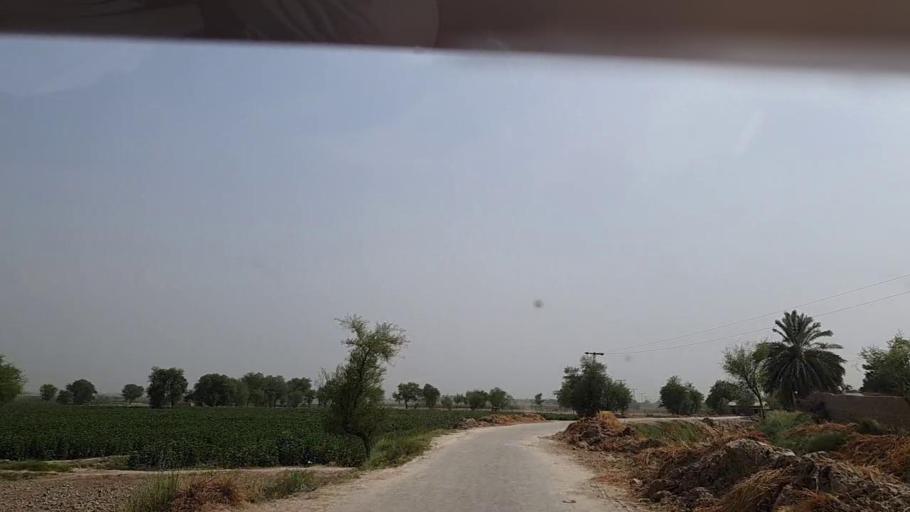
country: PK
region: Sindh
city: Khairpur Nathan Shah
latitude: 27.0593
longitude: 67.6866
